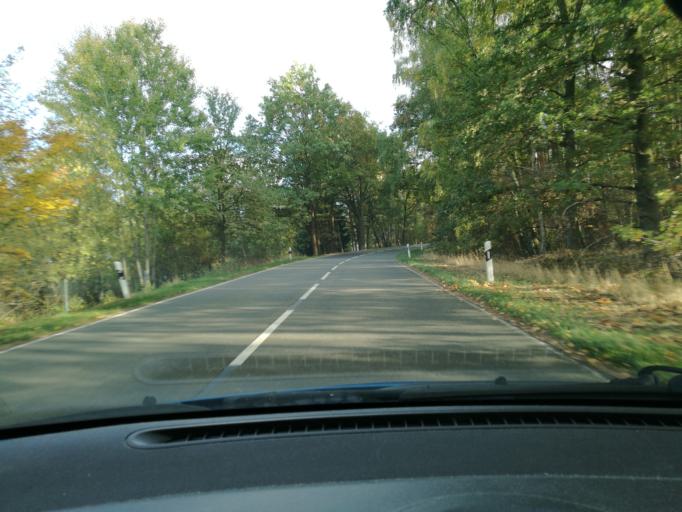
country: DE
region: Saxony-Anhalt
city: Luftkurort Arendsee
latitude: 52.8889
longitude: 11.4479
